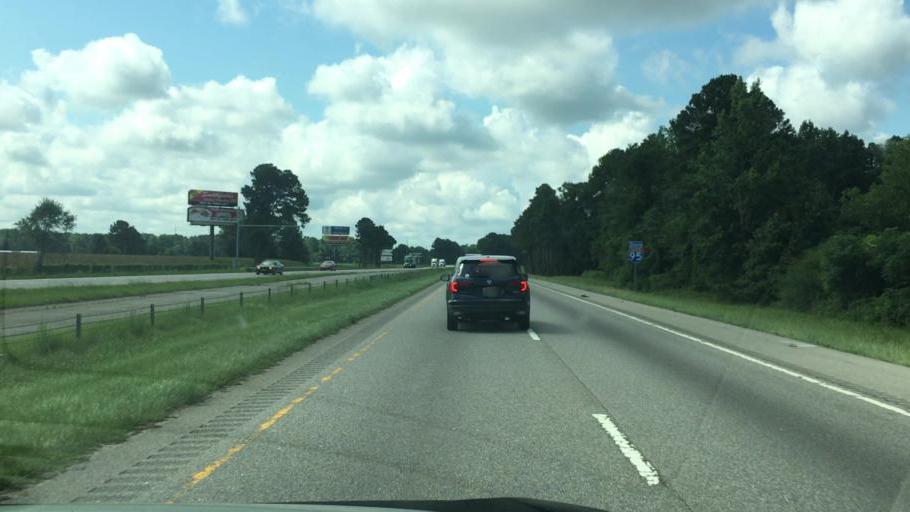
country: US
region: North Carolina
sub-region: Robeson County
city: Lumberton
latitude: 34.6986
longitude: -78.9985
